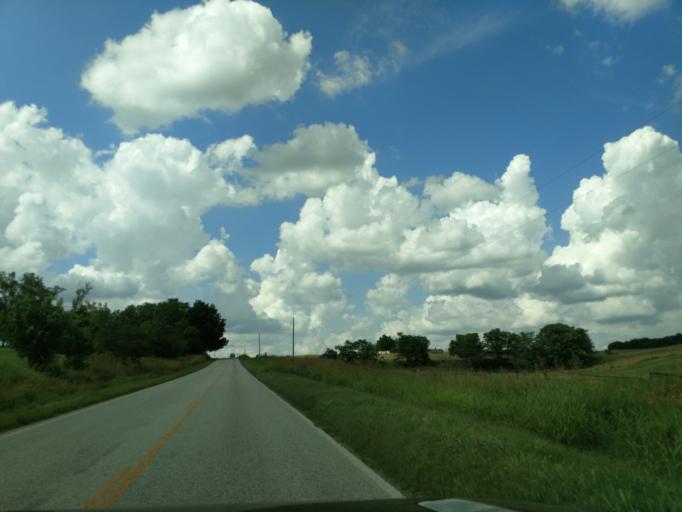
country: US
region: Arkansas
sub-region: Carroll County
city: Berryville
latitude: 36.4276
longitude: -93.5564
